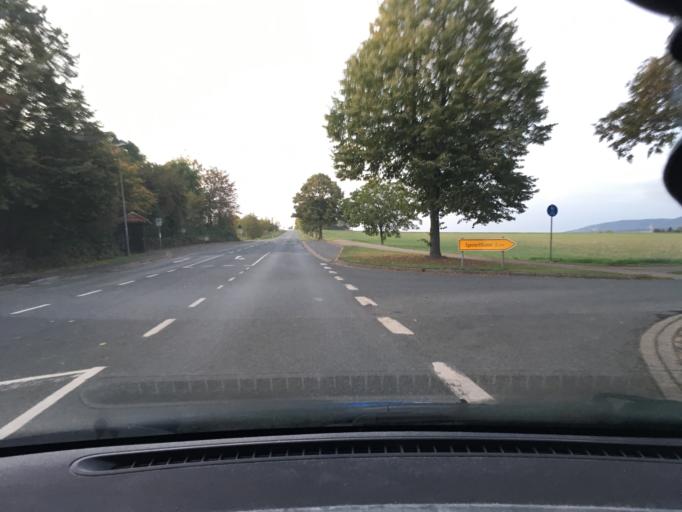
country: DE
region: Lower Saxony
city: Hulsede
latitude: 52.2108
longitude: 9.3928
